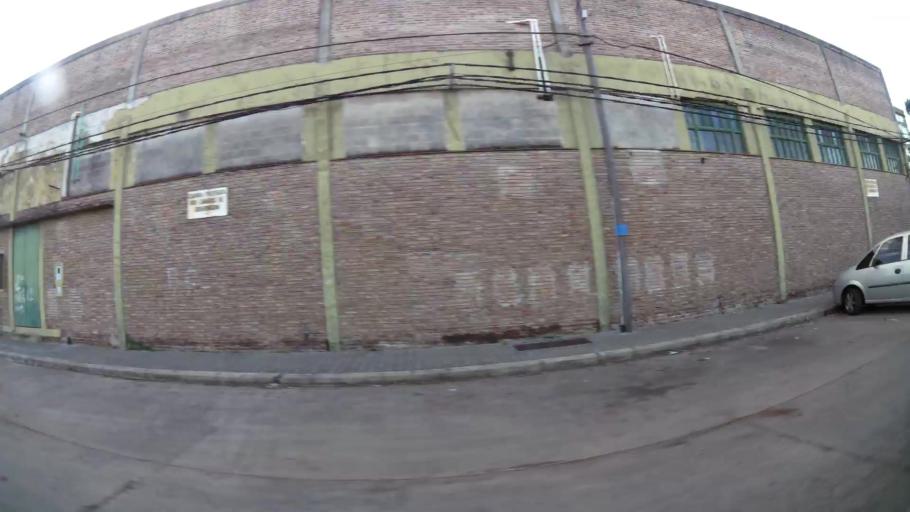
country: AR
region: Santa Fe
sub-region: Departamento de Rosario
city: Rosario
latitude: -32.9736
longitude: -60.6665
